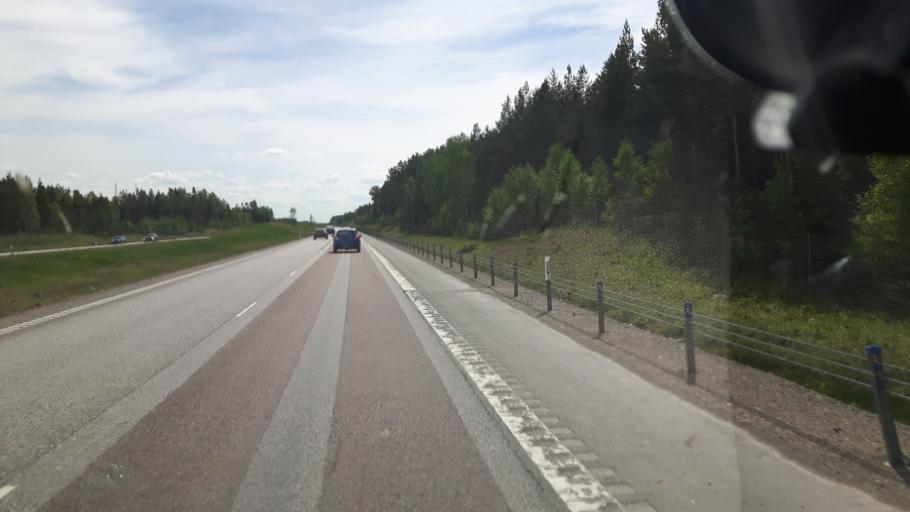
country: SE
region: Uppsala
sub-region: Tierps Kommun
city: Tierp
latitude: 60.2613
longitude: 17.4998
